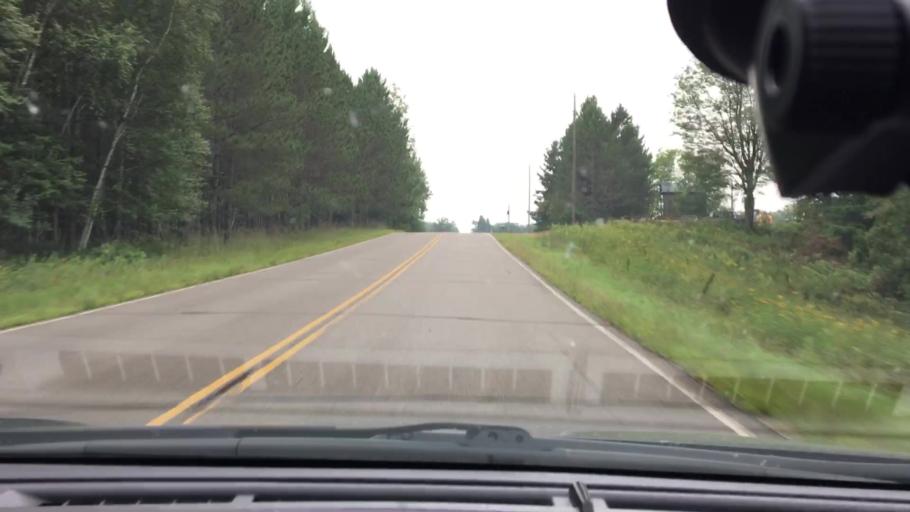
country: US
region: Minnesota
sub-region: Crow Wing County
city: Cross Lake
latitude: 46.6496
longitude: -94.0095
